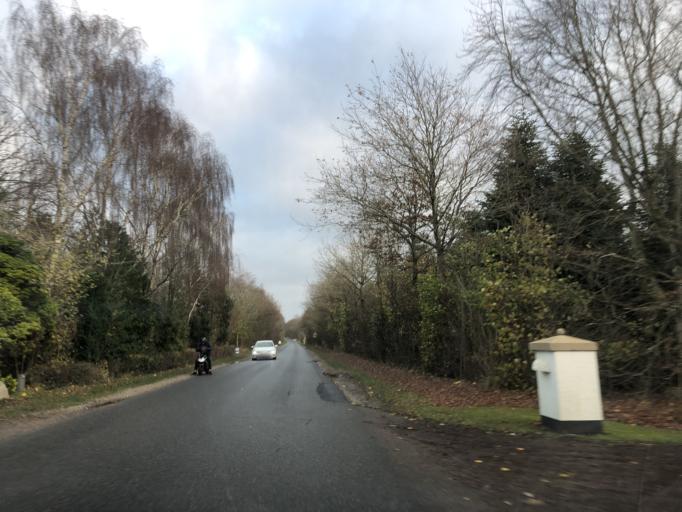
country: DK
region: Central Jutland
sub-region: Viborg Kommune
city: Viborg
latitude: 56.4755
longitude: 9.3442
